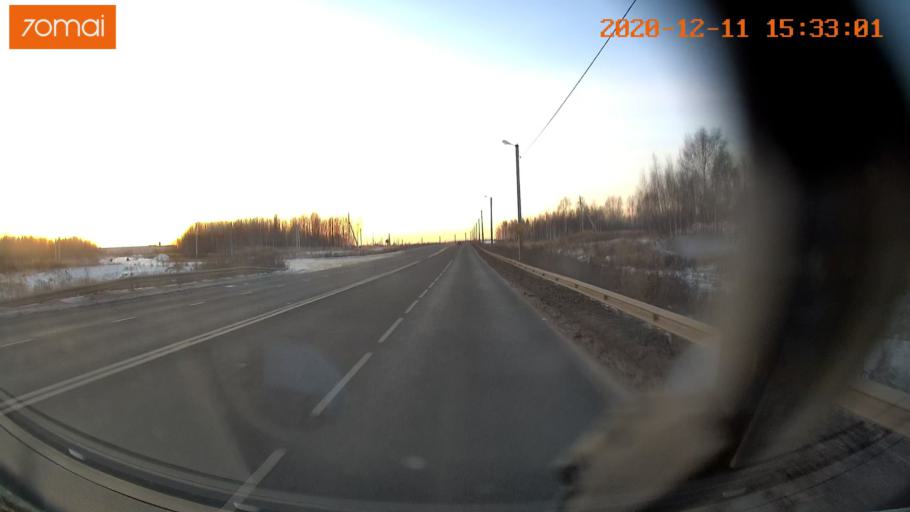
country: RU
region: Ivanovo
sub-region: Gorod Ivanovo
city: Ivanovo
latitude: 57.0528
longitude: 40.9560
